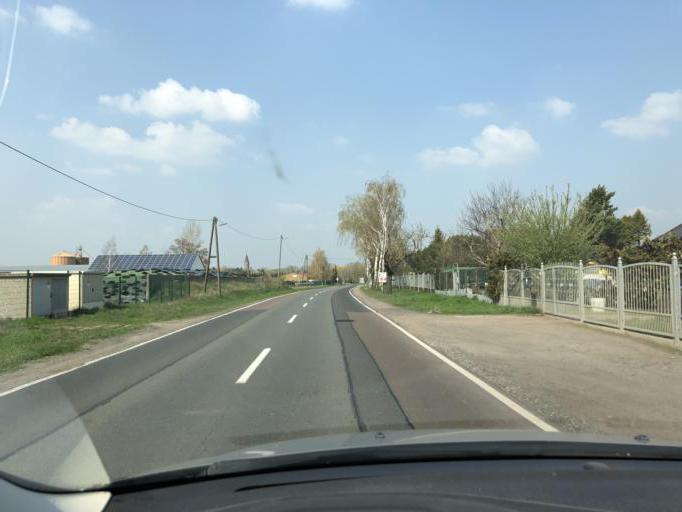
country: DE
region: Saxony-Anhalt
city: Zorbig
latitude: 51.6180
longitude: 12.1232
